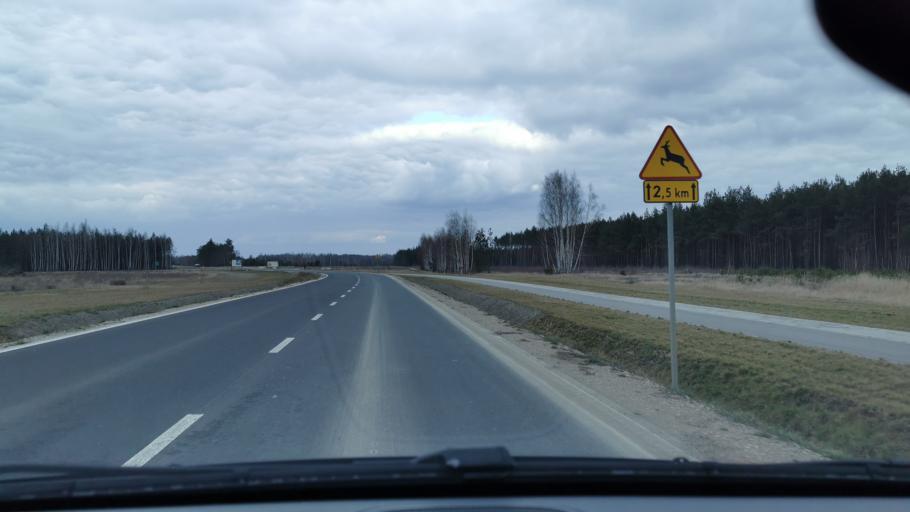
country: PL
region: Masovian Voivodeship
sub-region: Powiat zyrardowski
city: Zyrardow
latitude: 51.9930
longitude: 20.4646
